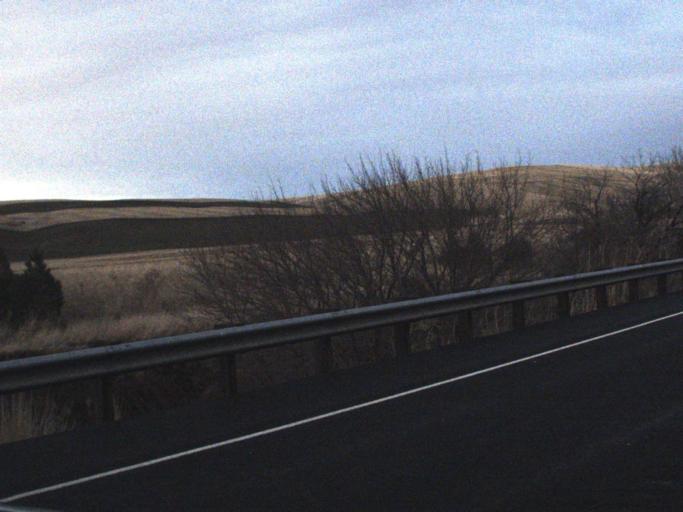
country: US
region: Washington
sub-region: Columbia County
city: Dayton
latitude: 46.5461
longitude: -117.8870
